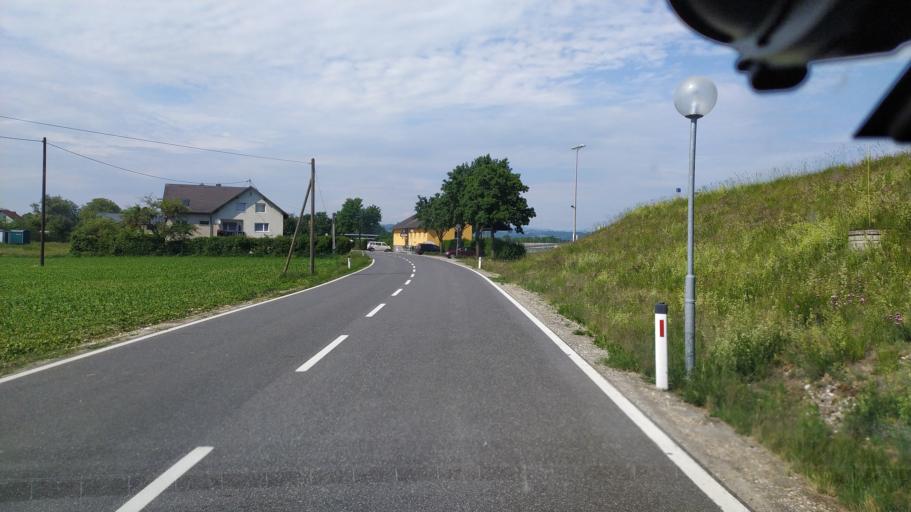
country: AT
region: Lower Austria
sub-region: Politischer Bezirk Amstetten
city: Strengberg
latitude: 48.1825
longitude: 14.7130
